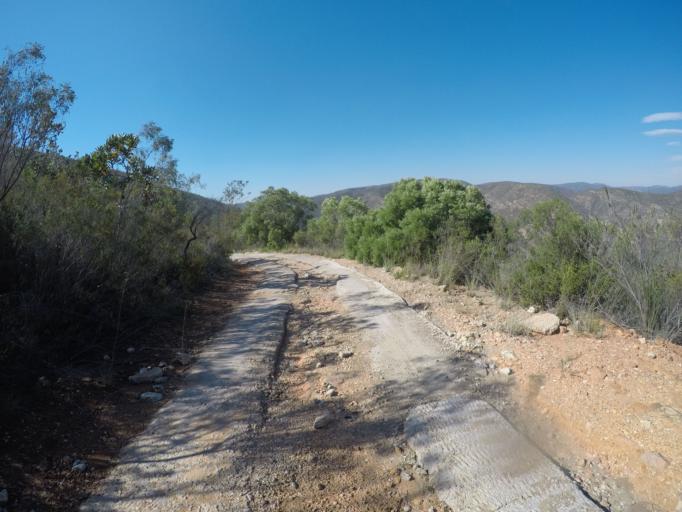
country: ZA
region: Eastern Cape
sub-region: Cacadu District Municipality
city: Kareedouw
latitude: -33.6396
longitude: 24.4526
